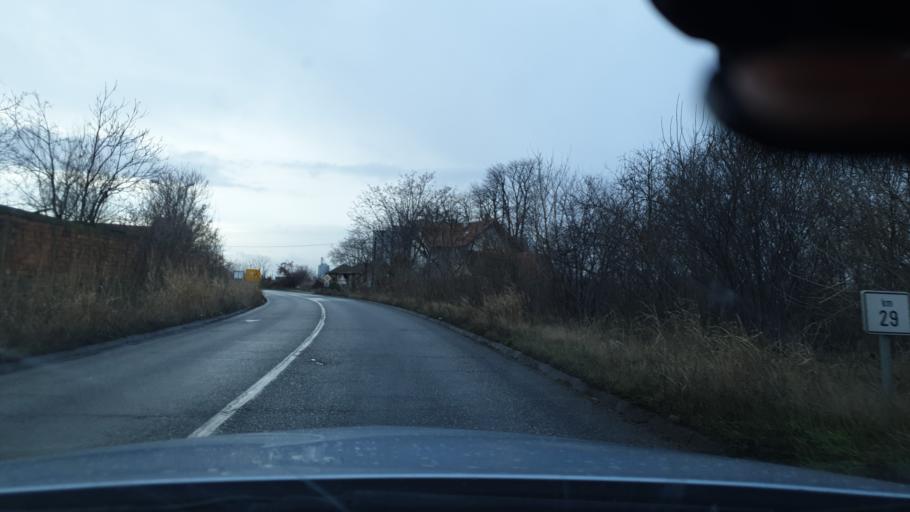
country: RS
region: Autonomna Pokrajina Vojvodina
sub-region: Juznobanatski Okrug
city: Kovin
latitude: 44.7525
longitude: 20.9671
